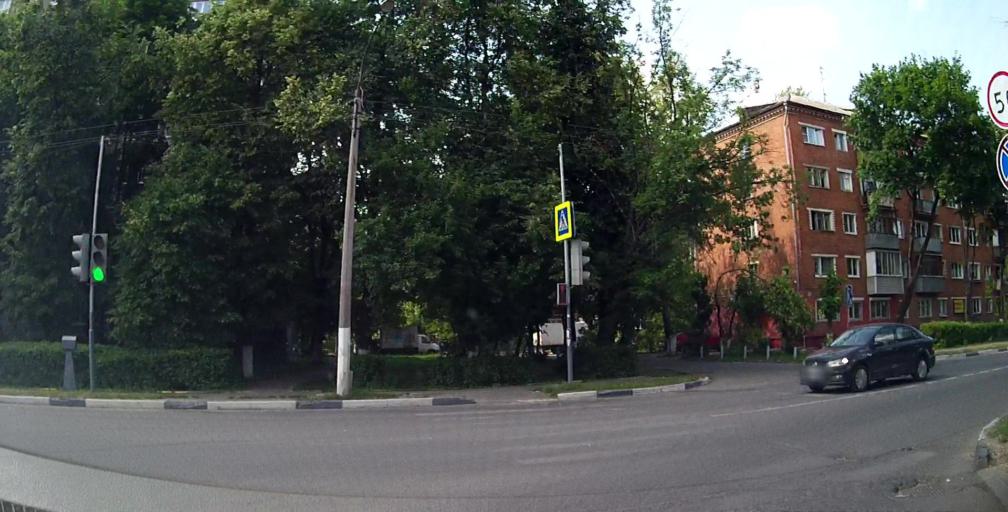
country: RU
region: Moskovskaya
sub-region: Podol'skiy Rayon
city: Podol'sk
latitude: 55.4157
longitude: 37.5308
